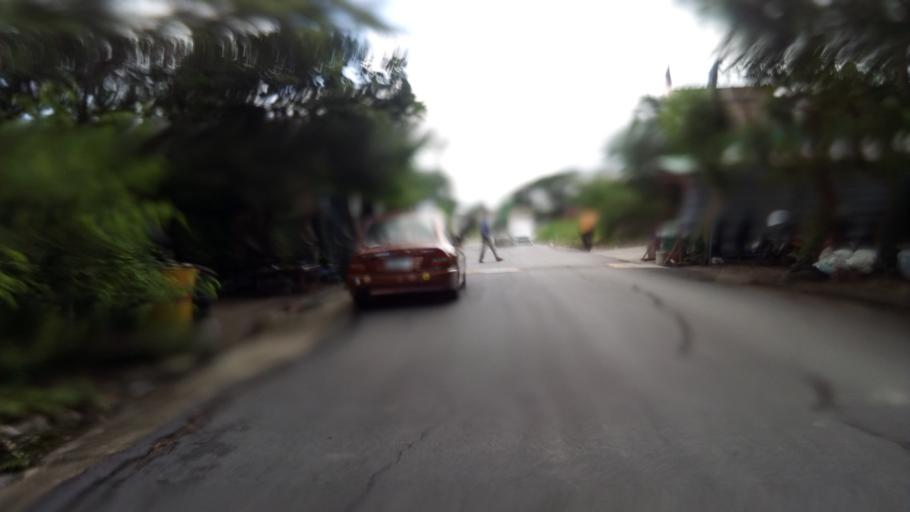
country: TH
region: Pathum Thani
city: Nong Suea
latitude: 14.0647
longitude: 100.8631
